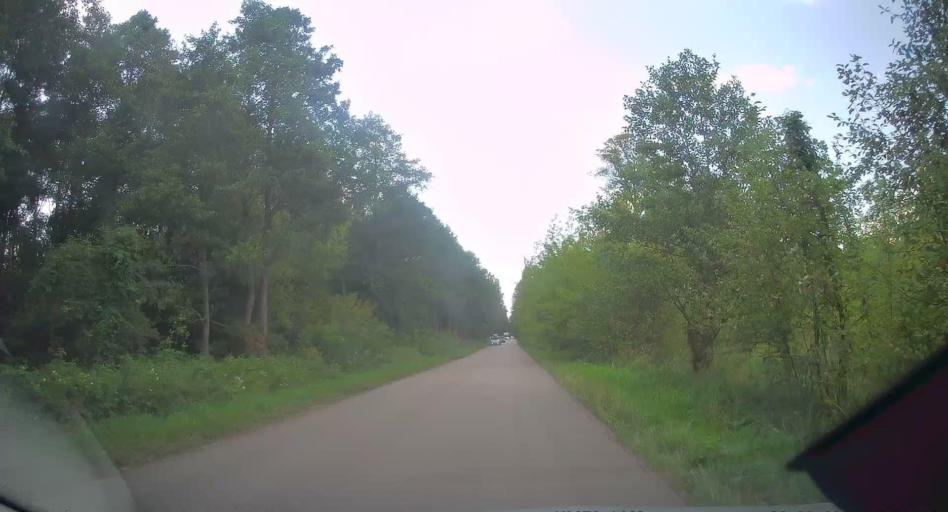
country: PL
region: Swietokrzyskie
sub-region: Powiat konecki
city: Ruda Maleniecka
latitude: 51.1383
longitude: 20.2429
